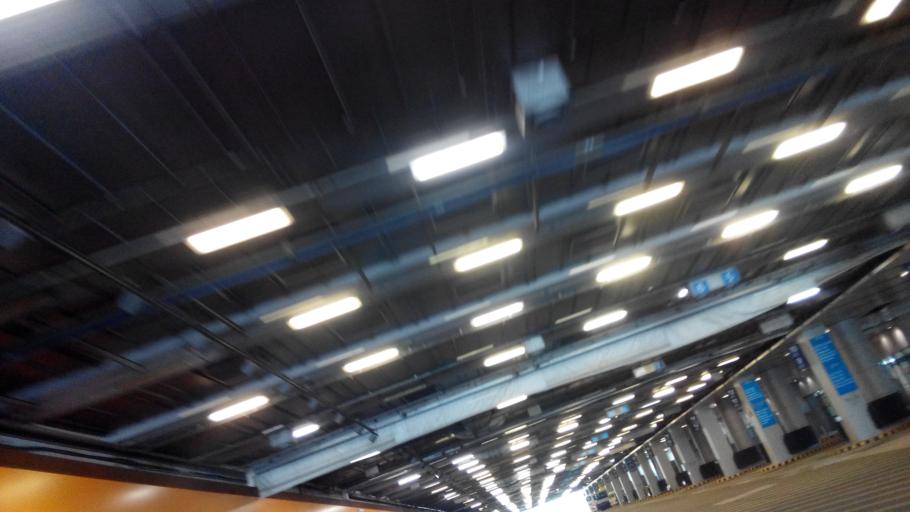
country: HK
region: Tuen Mun
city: Tuen Mun
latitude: 22.3171
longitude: 113.9372
